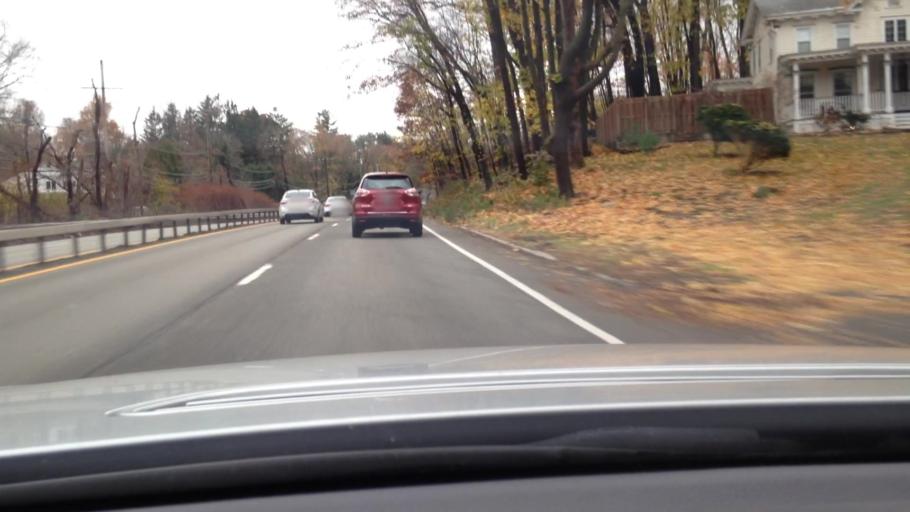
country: US
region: New York
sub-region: Westchester County
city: Briarcliff Manor
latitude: 41.1560
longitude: -73.8343
